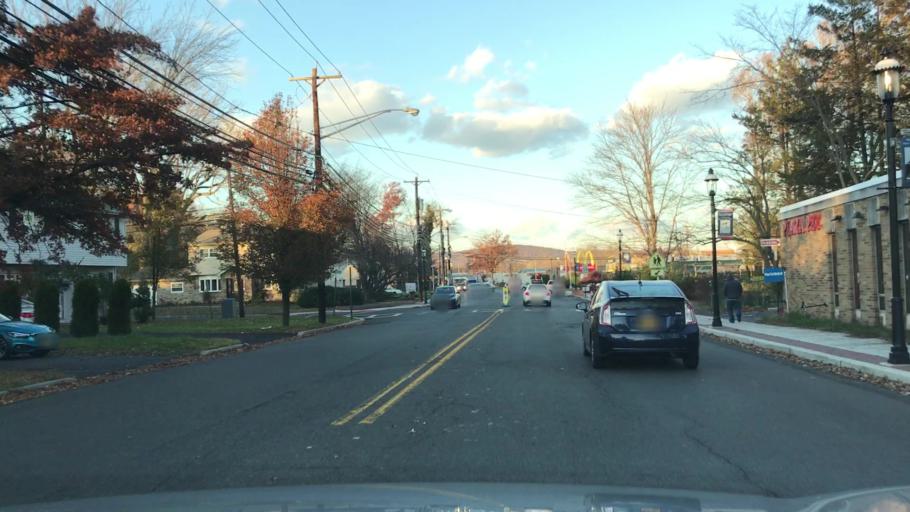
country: US
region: New Jersey
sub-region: Bergen County
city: Northvale
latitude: 41.0097
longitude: -73.9474
